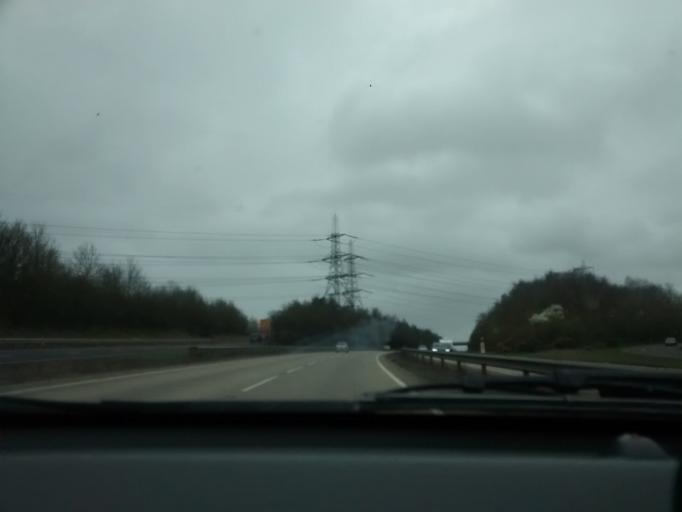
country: GB
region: England
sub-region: Suffolk
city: Bramford
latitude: 52.0897
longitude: 1.1157
